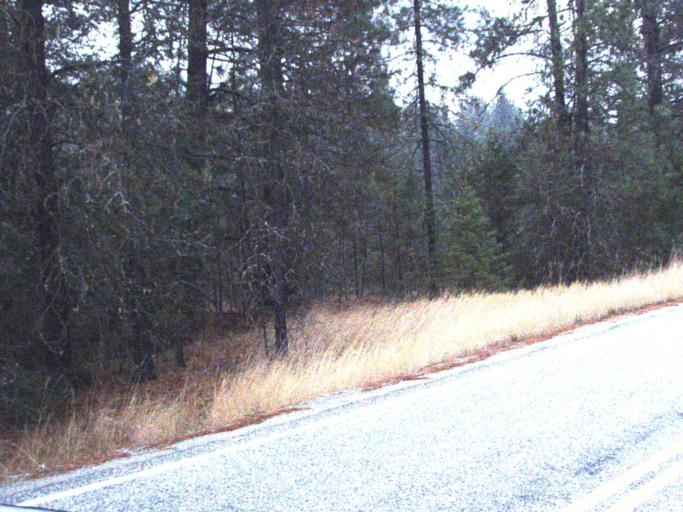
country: CA
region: British Columbia
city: Grand Forks
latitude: 48.9544
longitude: -118.2149
